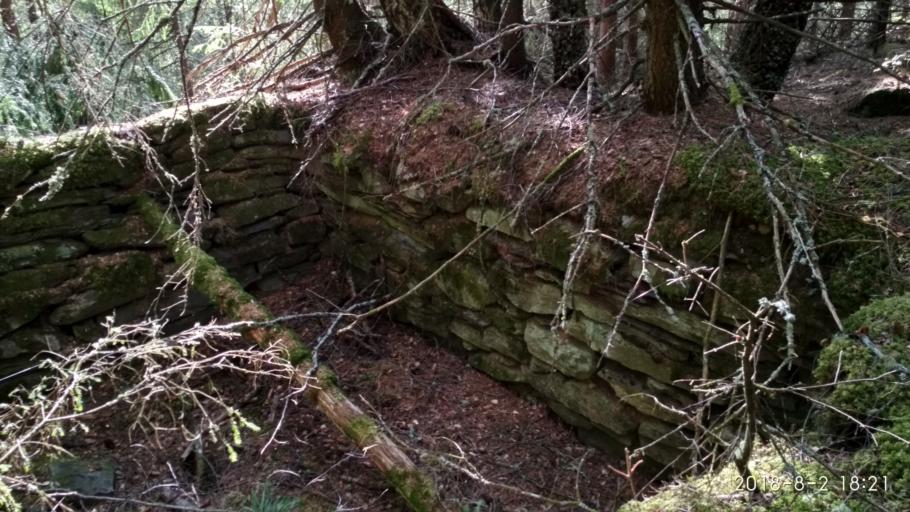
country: NO
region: Oppland
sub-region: Oyer
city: Tretten
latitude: 61.3719
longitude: 10.2896
